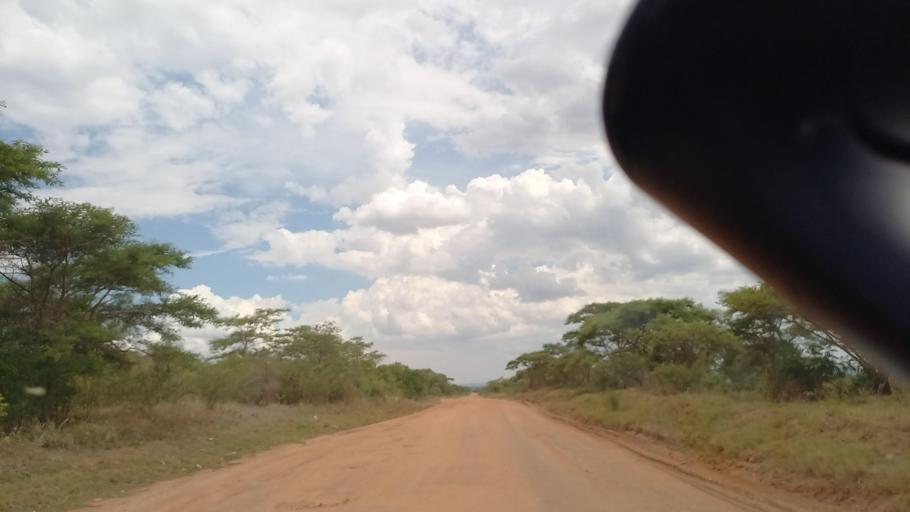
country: ZM
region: Southern
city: Nakambala
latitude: -16.0371
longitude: 27.9712
